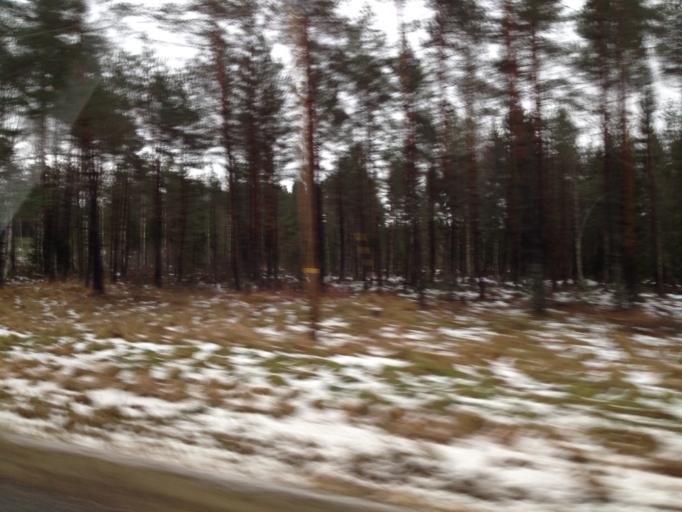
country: FI
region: Uusimaa
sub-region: Raaseporin
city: Ekenaes
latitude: 59.9656
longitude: 23.3773
